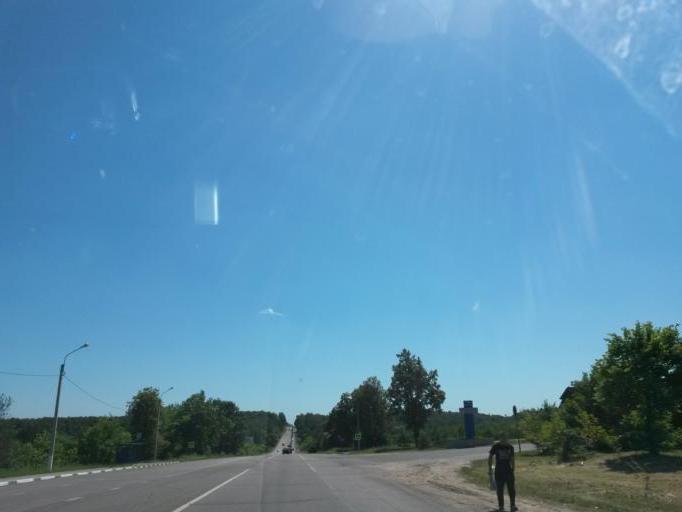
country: RU
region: Moskovskaya
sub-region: Chekhovskiy Rayon
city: Chekhov
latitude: 55.1144
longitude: 37.4479
